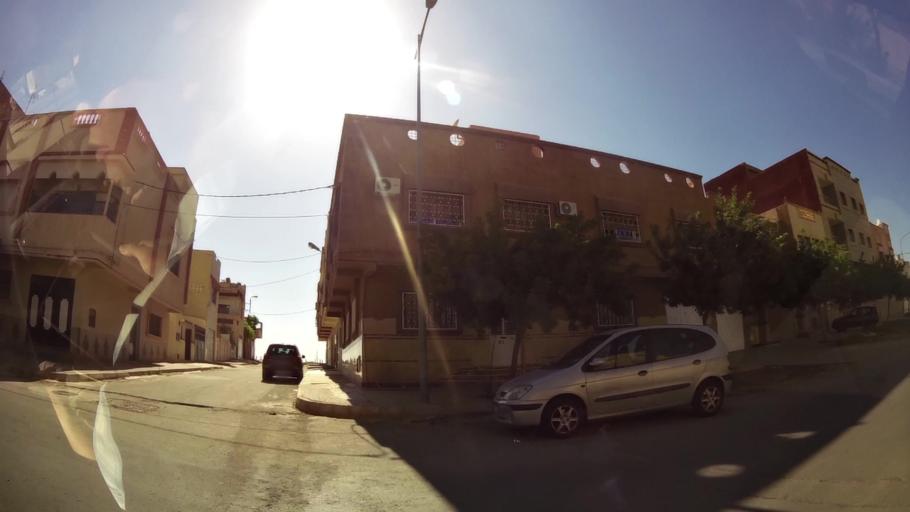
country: MA
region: Oriental
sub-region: Oujda-Angad
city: Oujda
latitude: 34.6942
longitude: -1.9215
